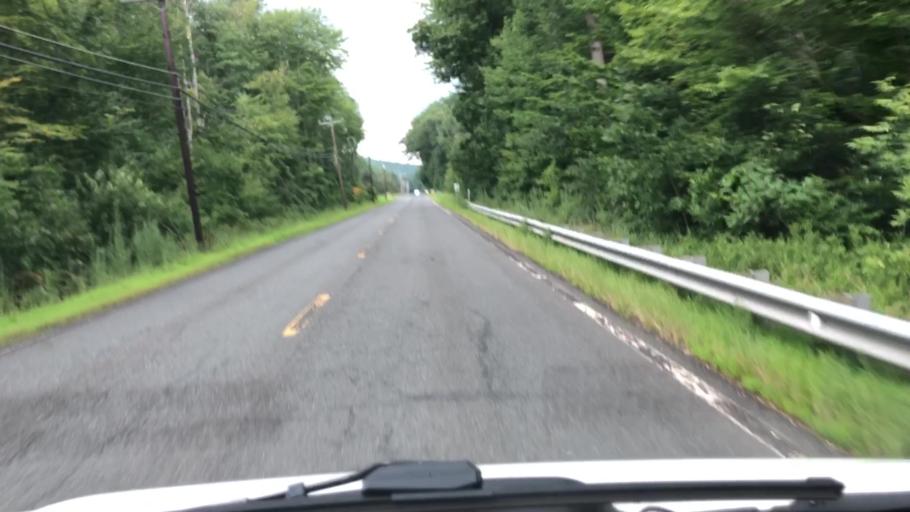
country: US
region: Massachusetts
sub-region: Franklin County
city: South Deerfield
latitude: 42.4865
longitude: -72.6219
